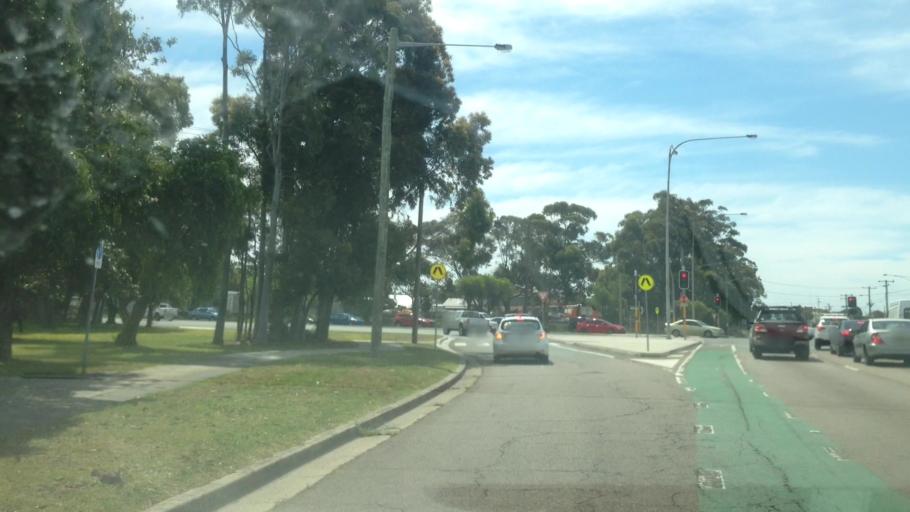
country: AU
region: New South Wales
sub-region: Newcastle
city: Broadmeadow
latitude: -32.9158
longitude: 151.7254
